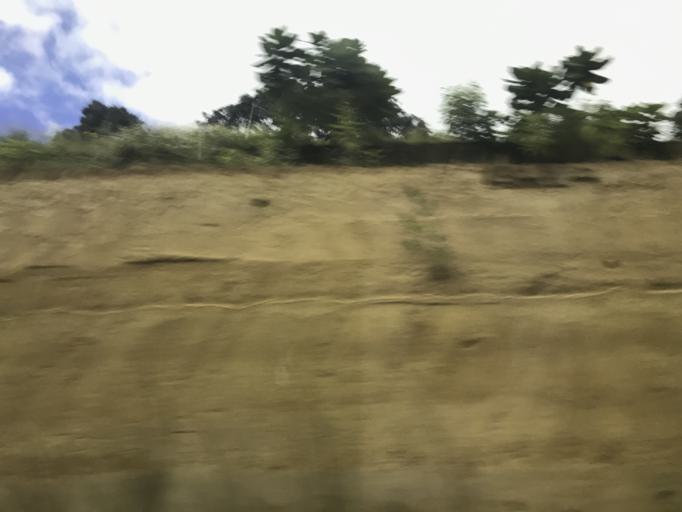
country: GT
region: Chimaltenango
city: El Tejar
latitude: 14.6298
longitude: -90.7928
